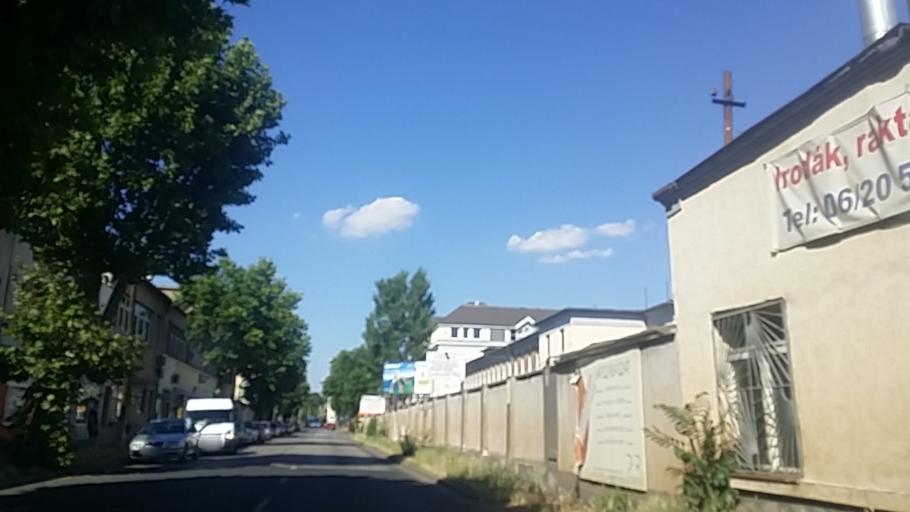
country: HU
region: Budapest
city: Budapest IV. keruelet
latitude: 47.5657
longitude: 19.0947
